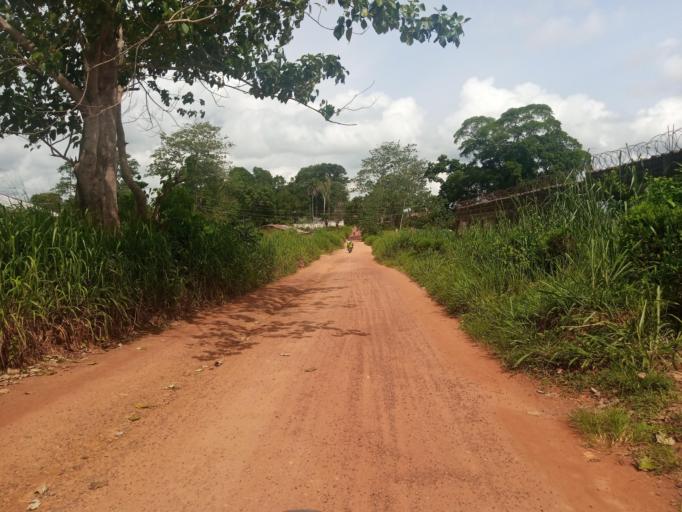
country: SL
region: Southern Province
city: Bo
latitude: 7.9689
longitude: -11.7517
